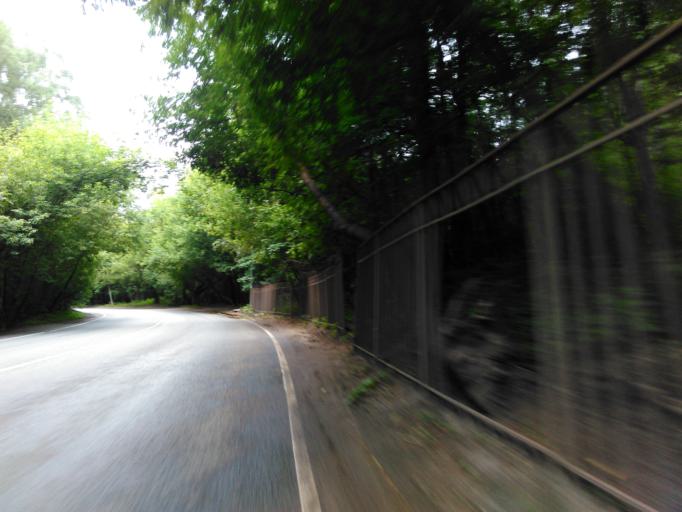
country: RU
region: Moskovskaya
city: Bogorodskoye
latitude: 55.8232
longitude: 37.6916
